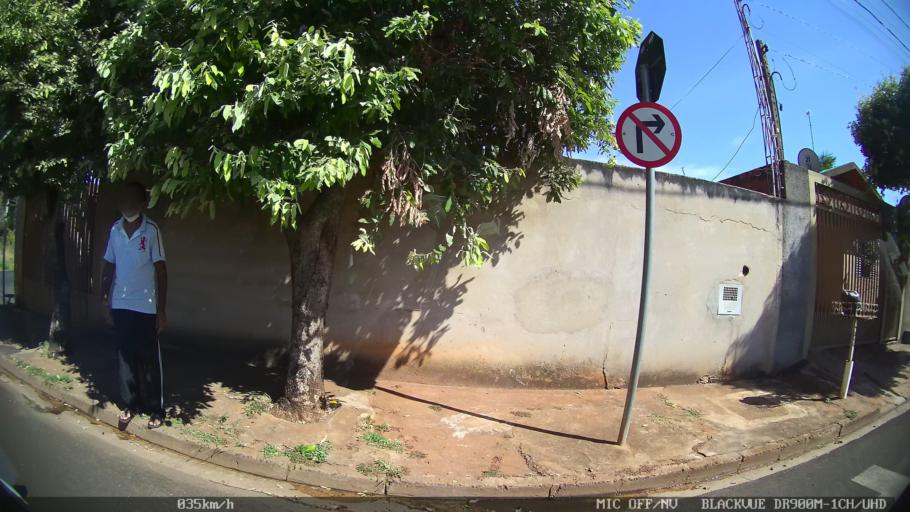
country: BR
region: Sao Paulo
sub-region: Sao Jose Do Rio Preto
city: Sao Jose do Rio Preto
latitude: -20.7689
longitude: -49.3983
